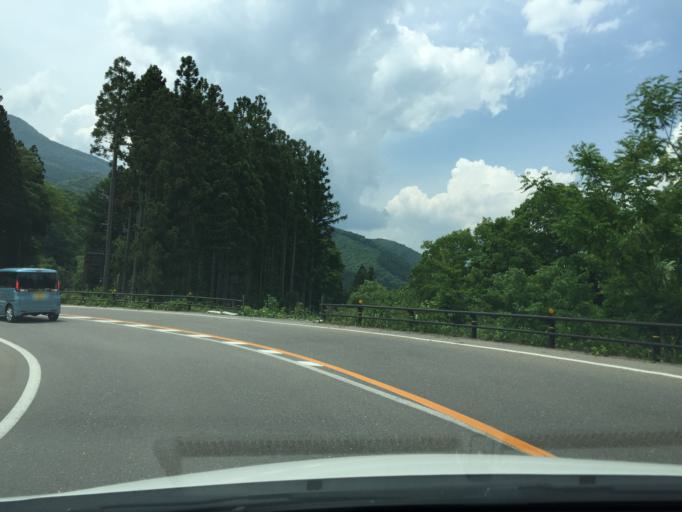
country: JP
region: Fukushima
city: Inawashiro
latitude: 37.6065
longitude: 140.1252
